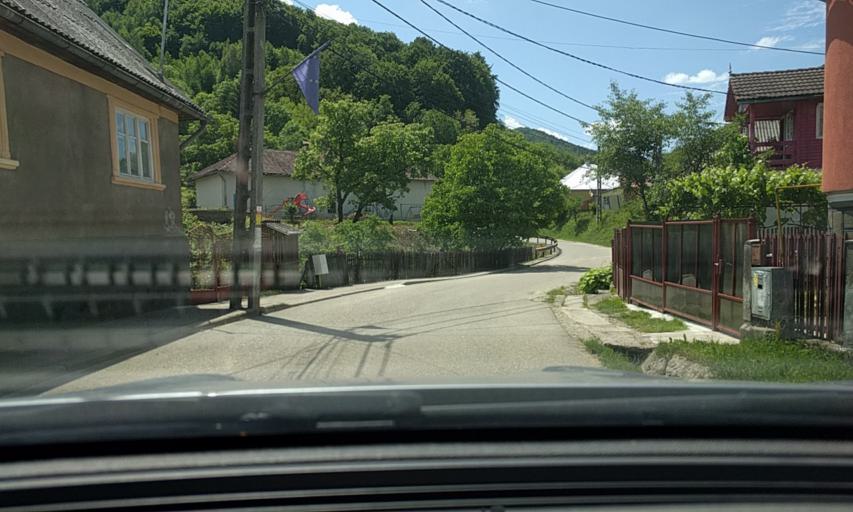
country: RO
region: Bistrita-Nasaud
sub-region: Oras Nasaud
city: Nasaud
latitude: 47.2784
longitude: 24.4048
